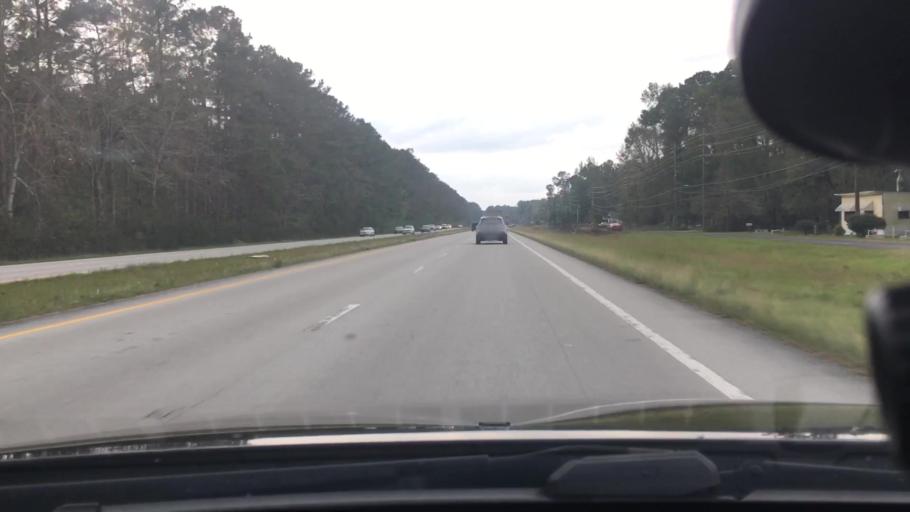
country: US
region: North Carolina
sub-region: Craven County
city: Neuse Forest
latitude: 34.9802
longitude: -76.9772
